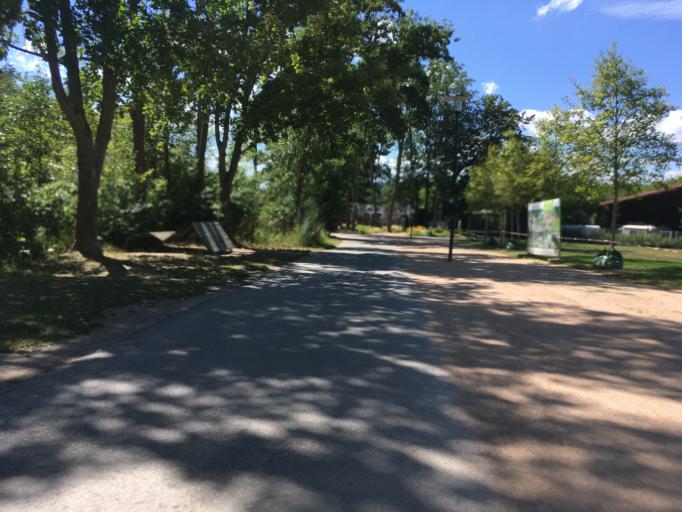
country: DE
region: Baden-Wuerttemberg
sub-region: Karlsruhe Region
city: Muhlacker
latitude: 48.9451
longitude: 8.8379
